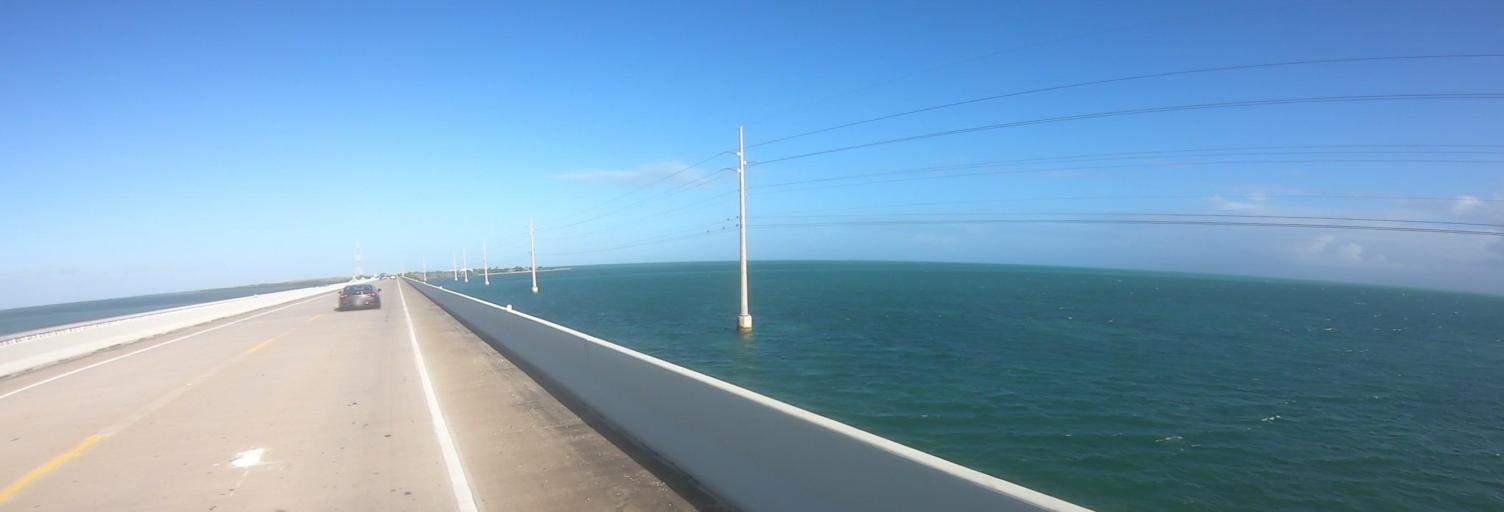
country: US
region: Florida
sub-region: Monroe County
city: Big Pine Key
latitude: 24.6475
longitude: -81.3230
